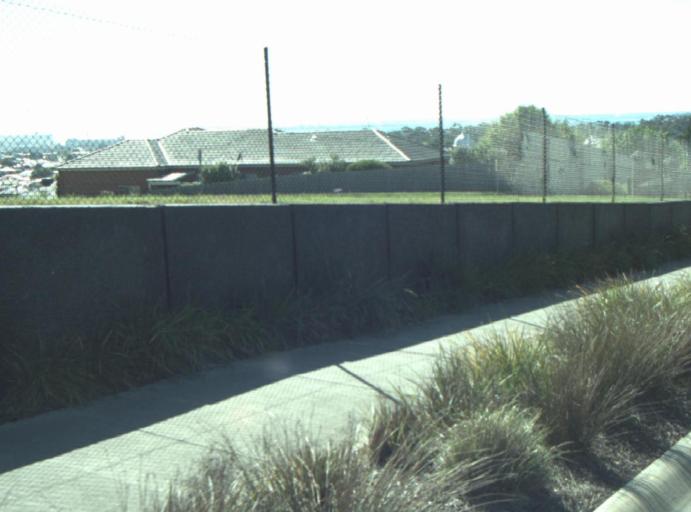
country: AU
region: Victoria
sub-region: Greater Geelong
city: Hamlyn Heights
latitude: -38.1126
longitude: 144.3276
